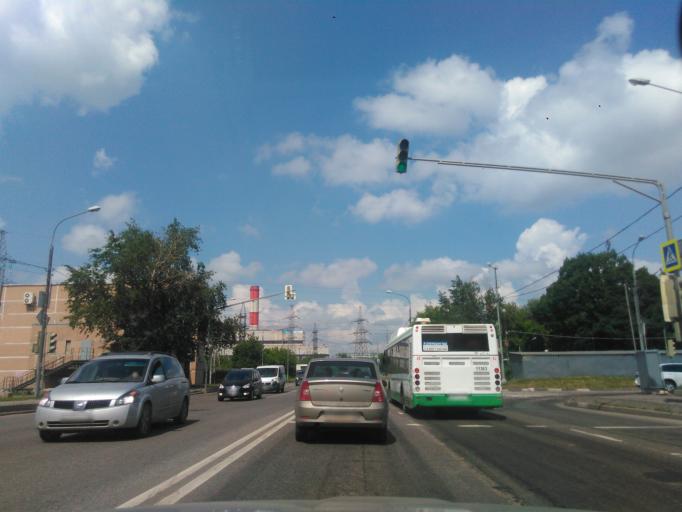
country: RU
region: Moscow
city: Businovo
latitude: 55.8871
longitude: 37.5139
